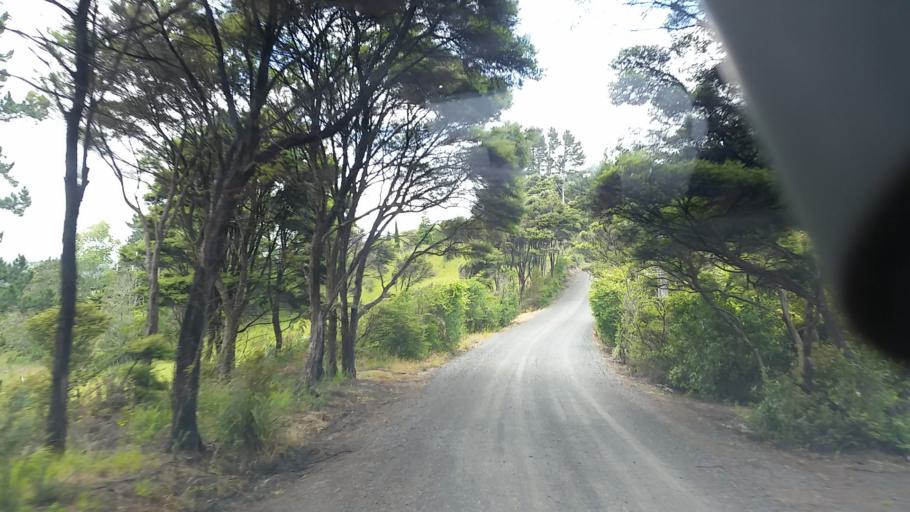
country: NZ
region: Auckland
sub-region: Auckland
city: Waitakere
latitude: -36.8853
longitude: 174.5865
